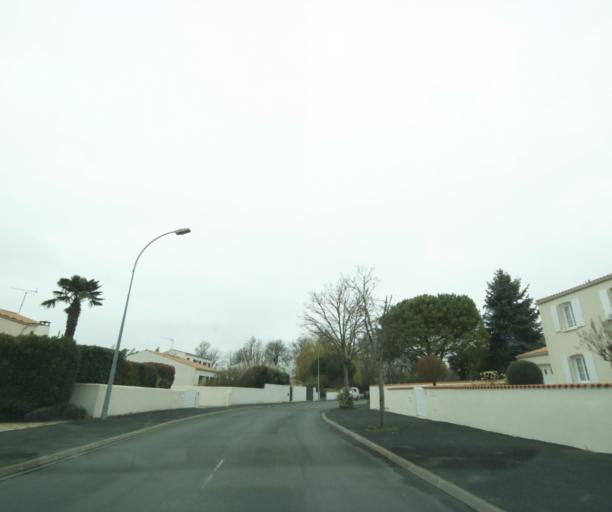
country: FR
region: Poitou-Charentes
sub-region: Departement de la Charente-Maritime
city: Lagord
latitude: 46.1882
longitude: -1.1402
